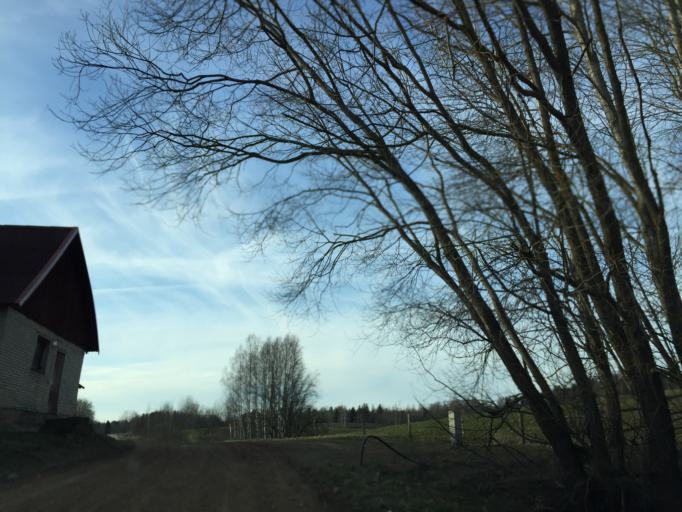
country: EE
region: Tartu
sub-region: Noo vald
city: Noo
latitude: 58.1338
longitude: 26.5950
